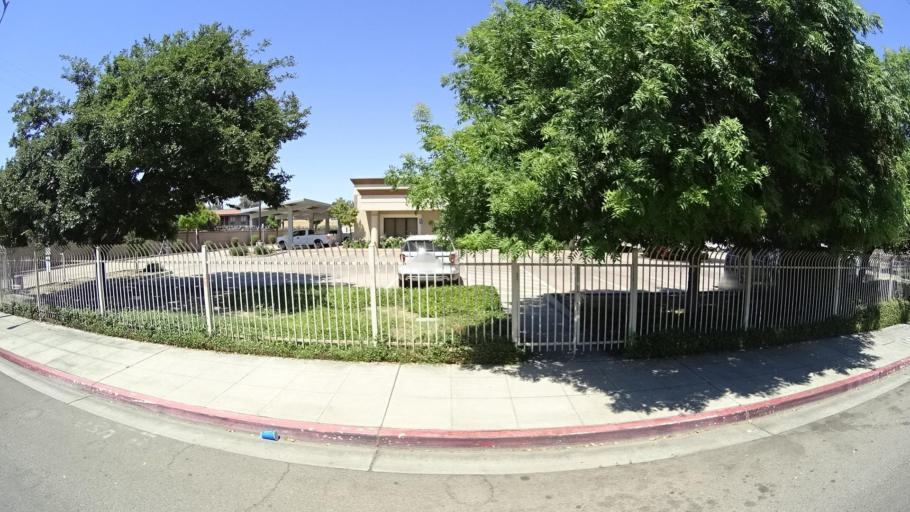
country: US
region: California
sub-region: Fresno County
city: Fresno
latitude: 36.7085
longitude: -119.7728
